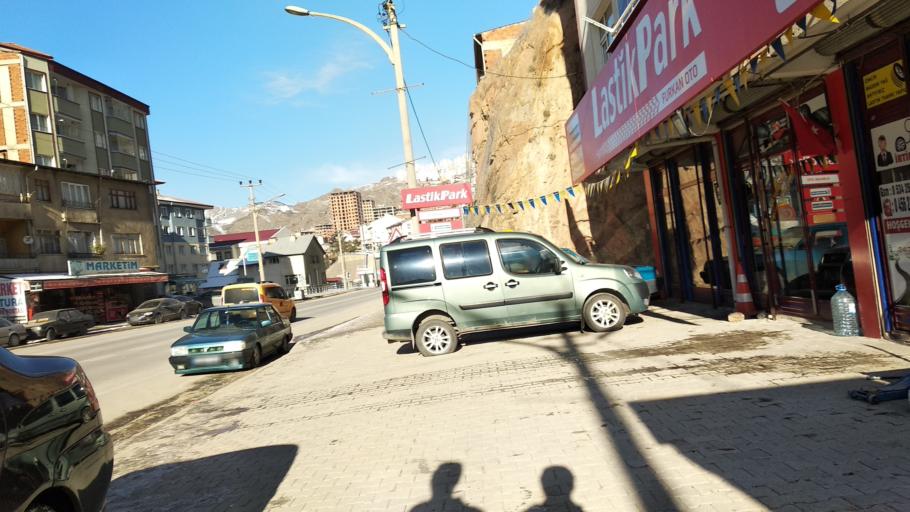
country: TR
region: Gumushane
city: Gumushkhane
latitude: 40.4560
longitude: 39.4904
